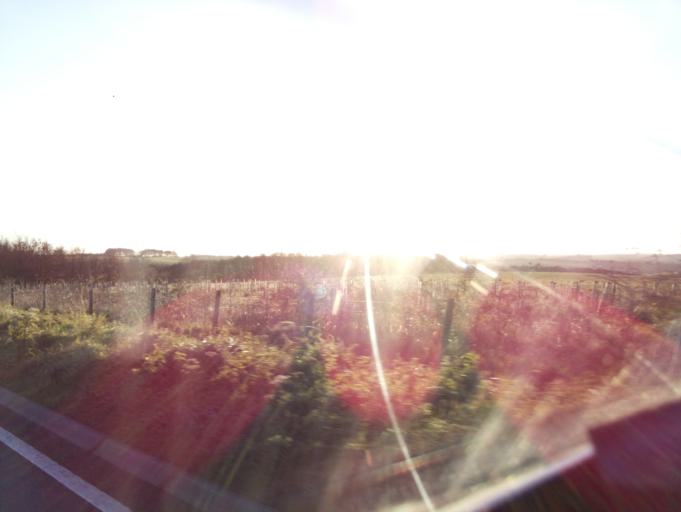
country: GB
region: England
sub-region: Wiltshire
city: Chicklade
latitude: 51.1319
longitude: -2.1621
